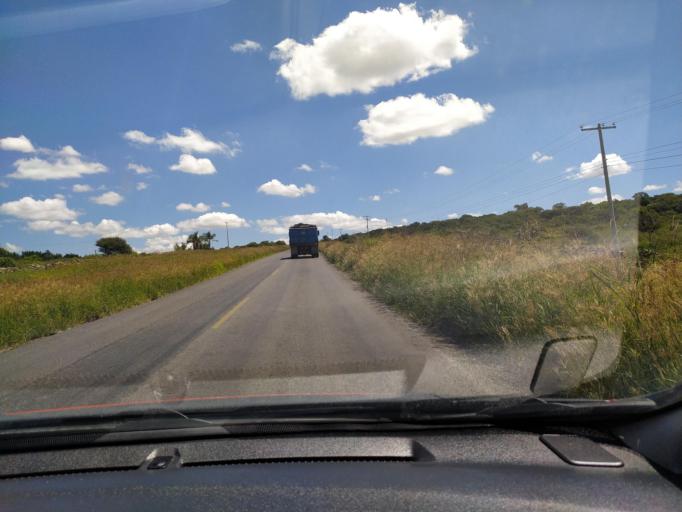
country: MX
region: Jalisco
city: San Diego de Alejandria
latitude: 21.0076
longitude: -102.0276
